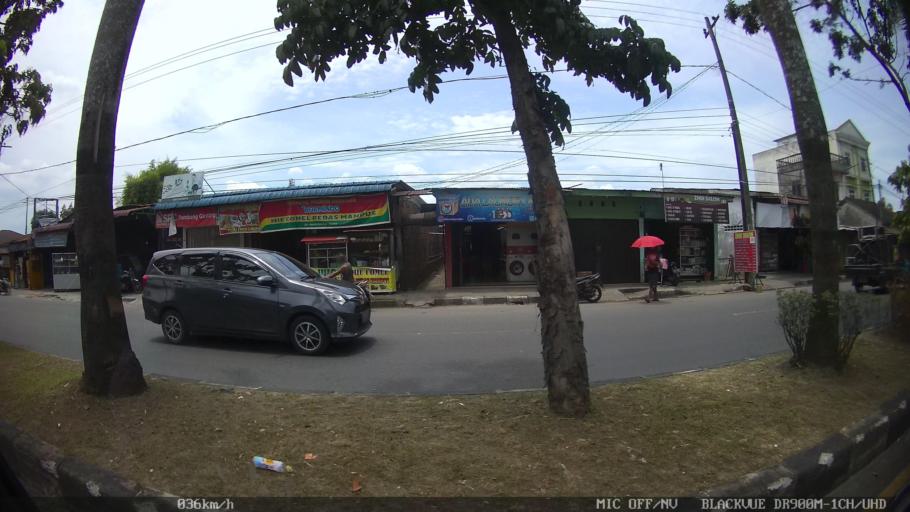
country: ID
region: North Sumatra
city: Deli Tua
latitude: 3.5325
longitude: 98.6456
